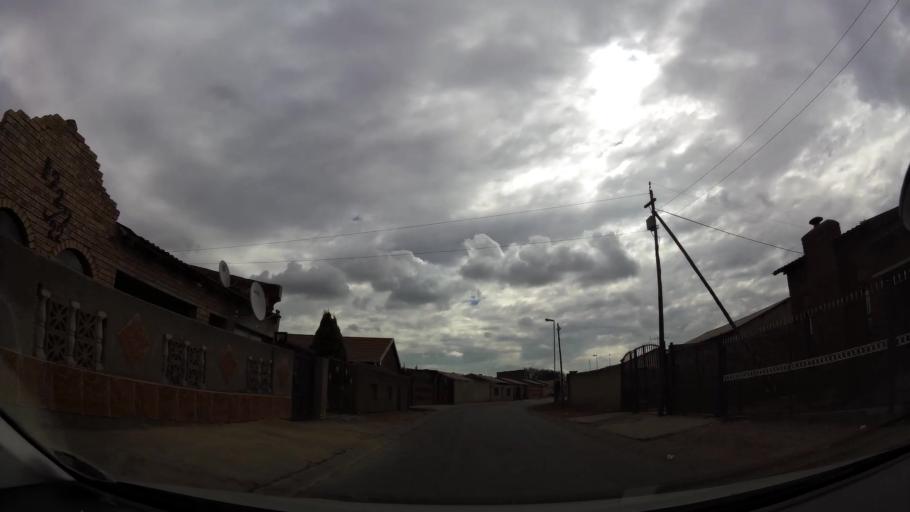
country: ZA
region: Gauteng
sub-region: City of Johannesburg Metropolitan Municipality
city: Soweto
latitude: -26.2762
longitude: 27.8602
